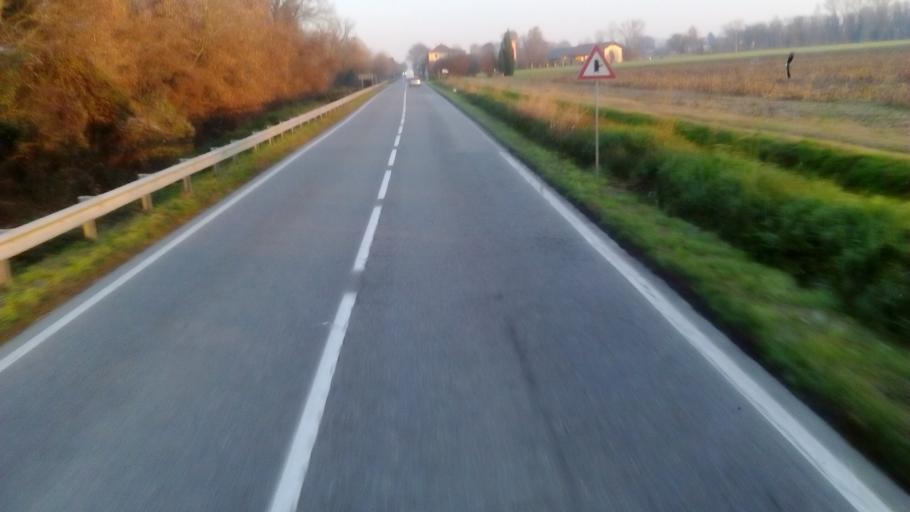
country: IT
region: Lombardy
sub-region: Provincia di Cremona
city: Romanengo
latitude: 45.3735
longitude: 9.8071
